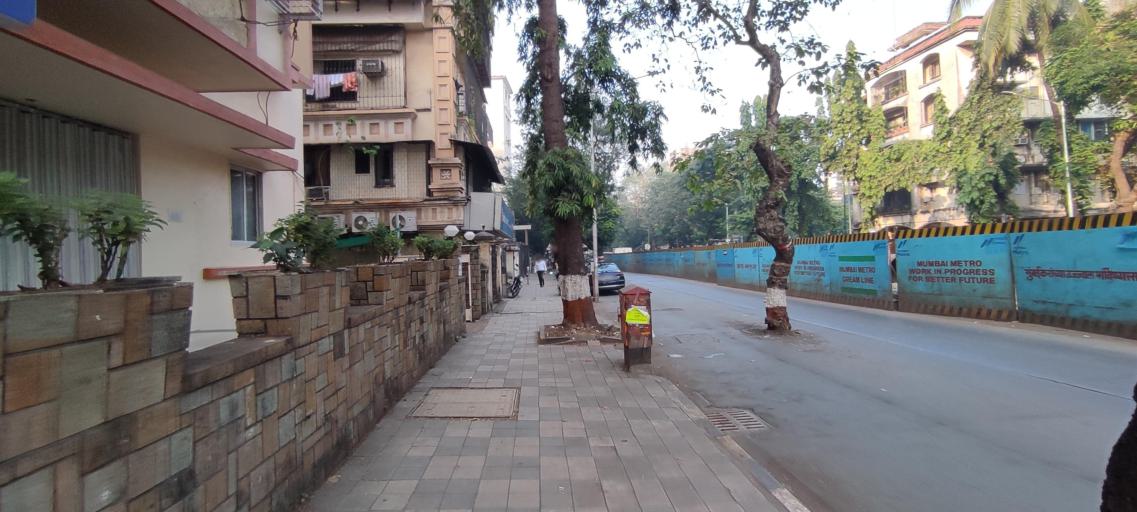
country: IN
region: Maharashtra
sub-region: Mumbai Suburban
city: Mumbai
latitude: 19.0717
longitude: 72.8374
